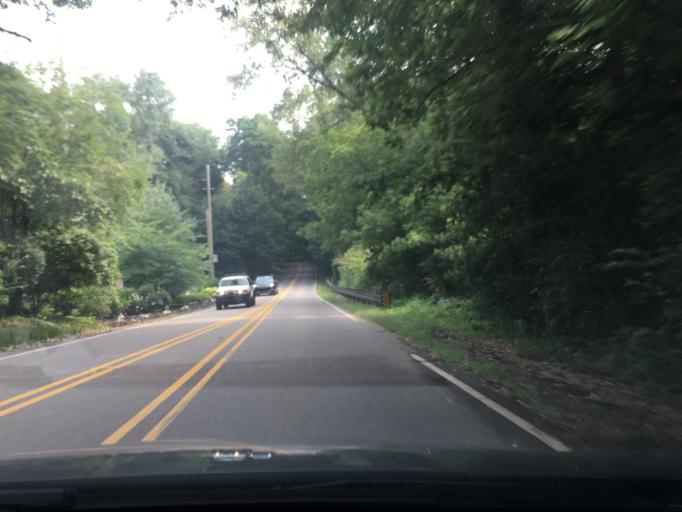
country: US
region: Michigan
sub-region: Oakland County
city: Bloomfield Hills
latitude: 42.5863
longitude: -83.2358
